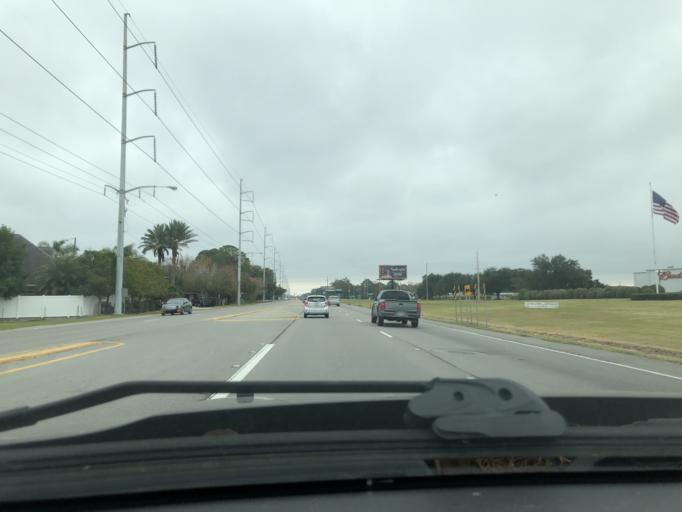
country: US
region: Louisiana
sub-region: Jefferson Parish
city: Elmwood
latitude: 29.9765
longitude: -90.1936
